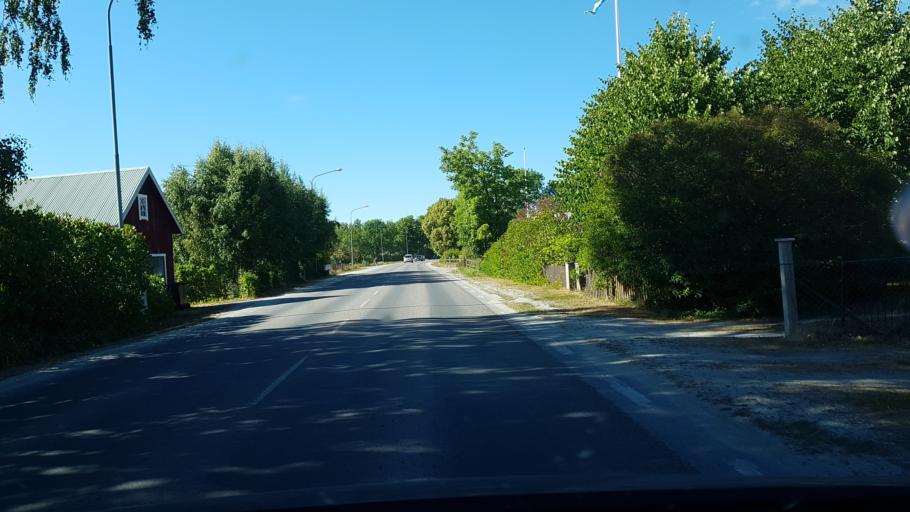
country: SE
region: Gotland
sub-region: Gotland
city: Klintehamn
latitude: 57.4360
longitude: 18.1455
